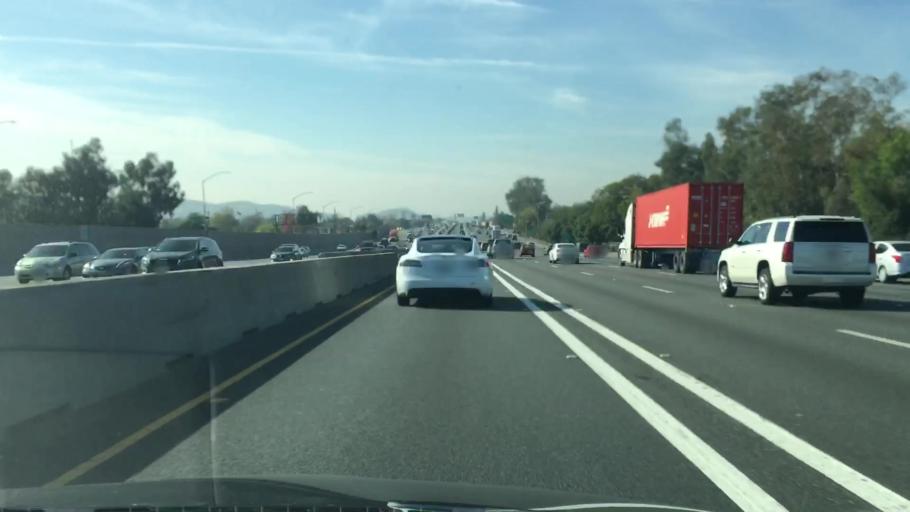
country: US
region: California
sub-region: Los Angeles County
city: Pomona
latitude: 34.0777
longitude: -117.7431
